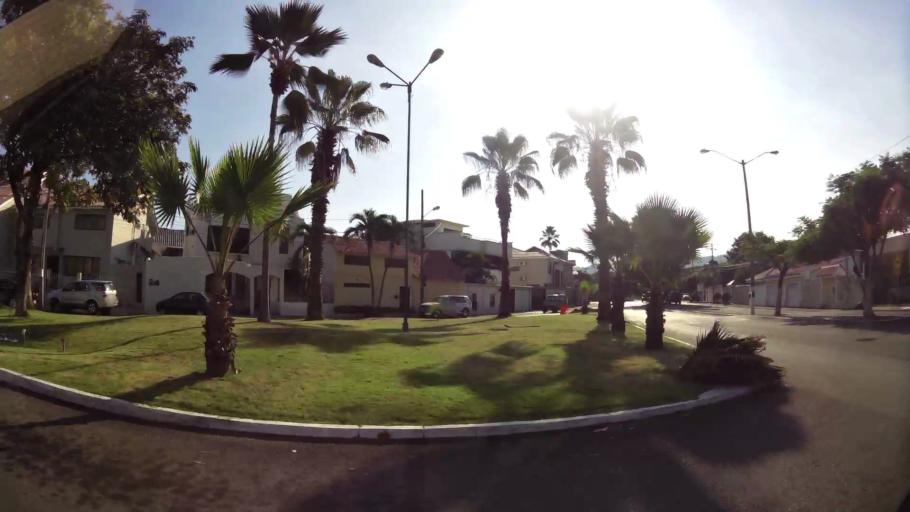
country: EC
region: Guayas
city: Santa Lucia
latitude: -2.1937
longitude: -79.9655
